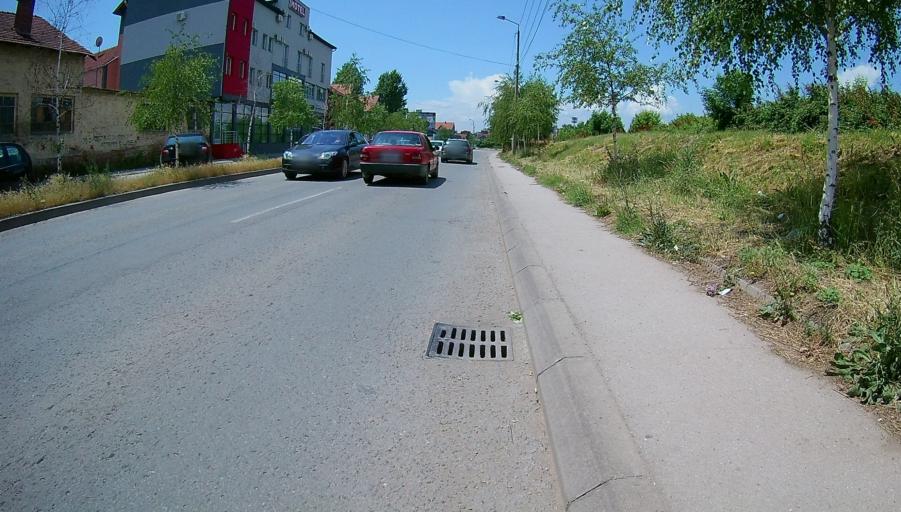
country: RS
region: Central Serbia
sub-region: Nisavski Okrug
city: Nis
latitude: 43.3120
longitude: 21.9088
